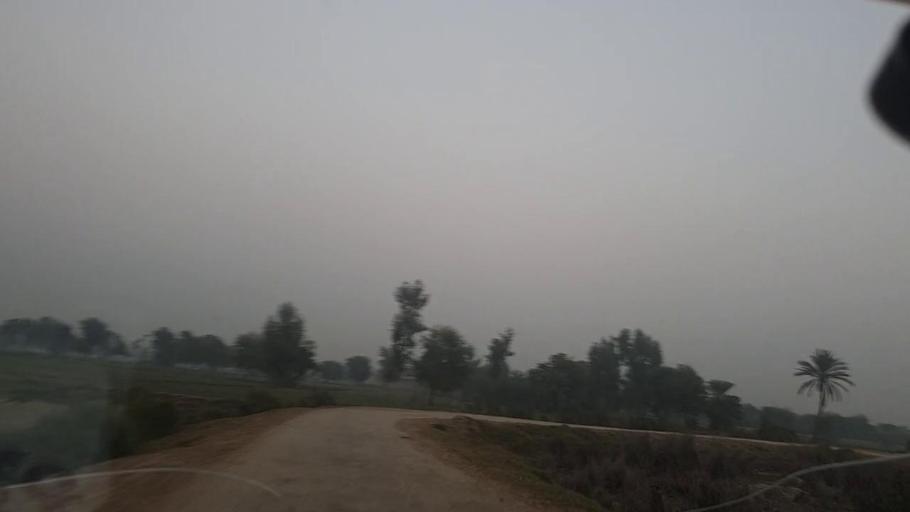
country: PK
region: Sindh
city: Hingorja
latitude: 27.2196
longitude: 68.4317
